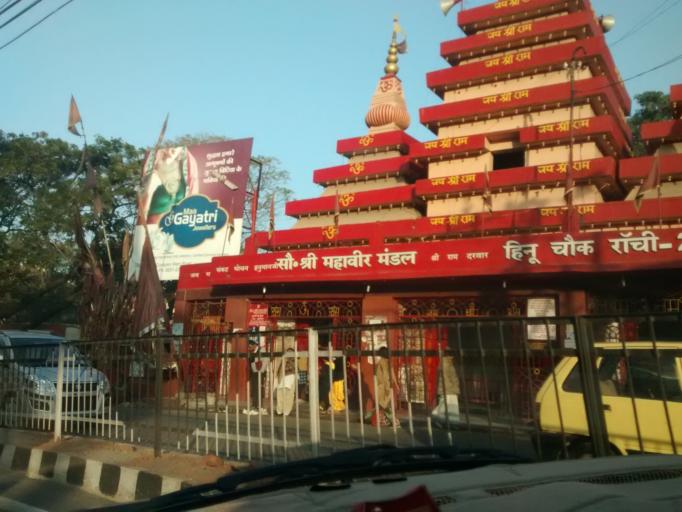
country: IN
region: Jharkhand
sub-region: Ranchi
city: Ranchi
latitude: 23.3282
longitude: 85.3151
